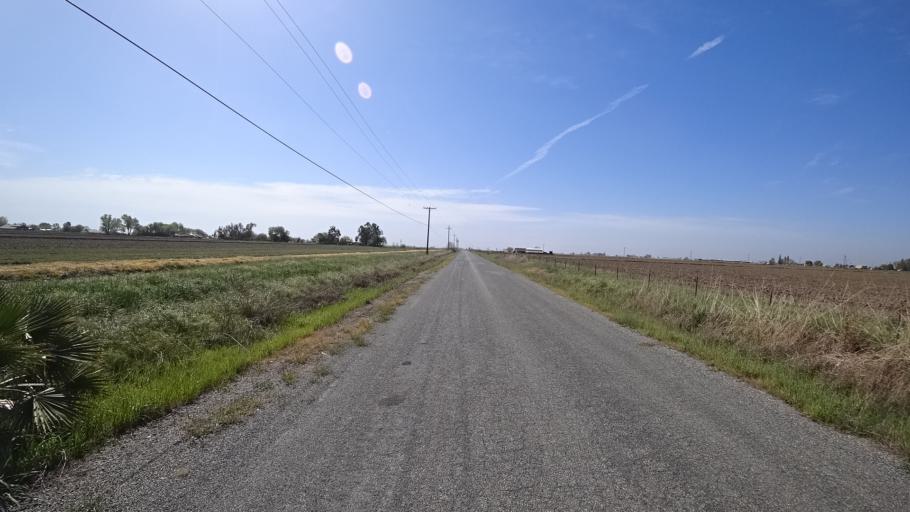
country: US
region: California
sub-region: Glenn County
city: Willows
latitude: 39.5863
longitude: -122.0557
